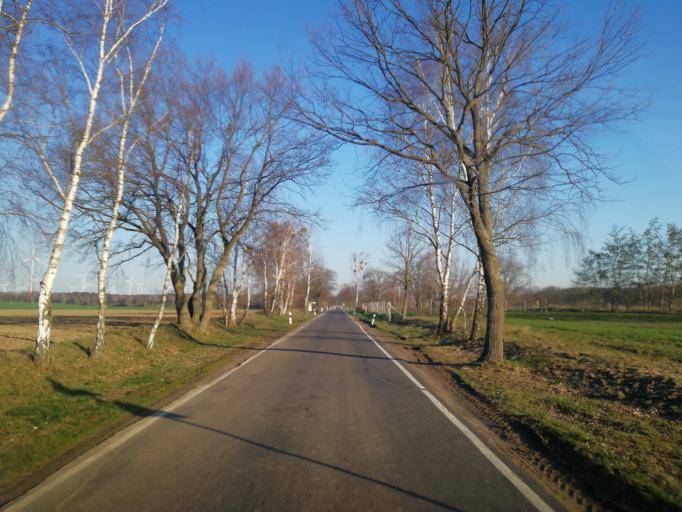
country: DE
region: Brandenburg
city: Drahnsdorf
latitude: 51.8559
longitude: 13.6012
